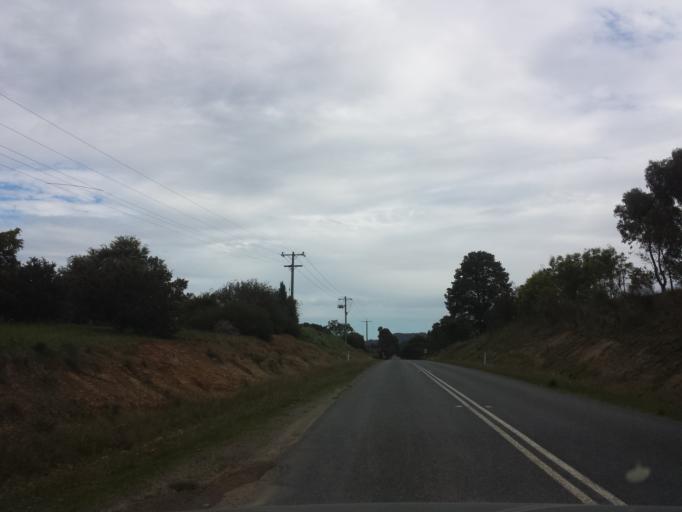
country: AU
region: Victoria
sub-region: Yarra Ranges
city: Yarra Glen
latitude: -37.6430
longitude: 145.3722
